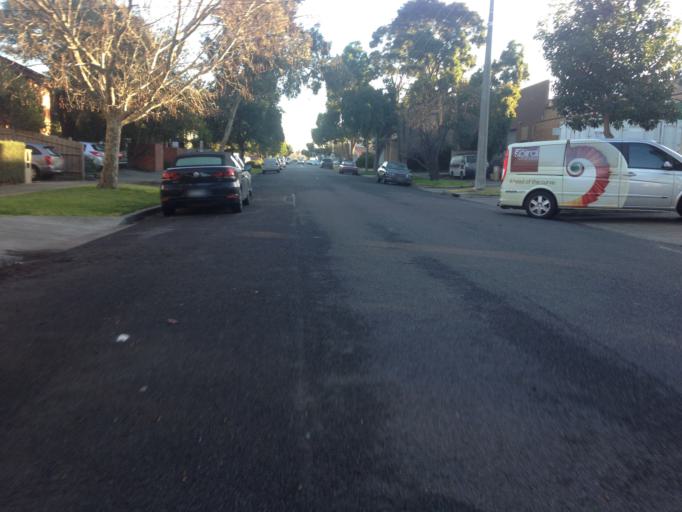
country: AU
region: Victoria
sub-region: Darebin
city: Fairfield
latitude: -37.7689
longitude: 145.0210
